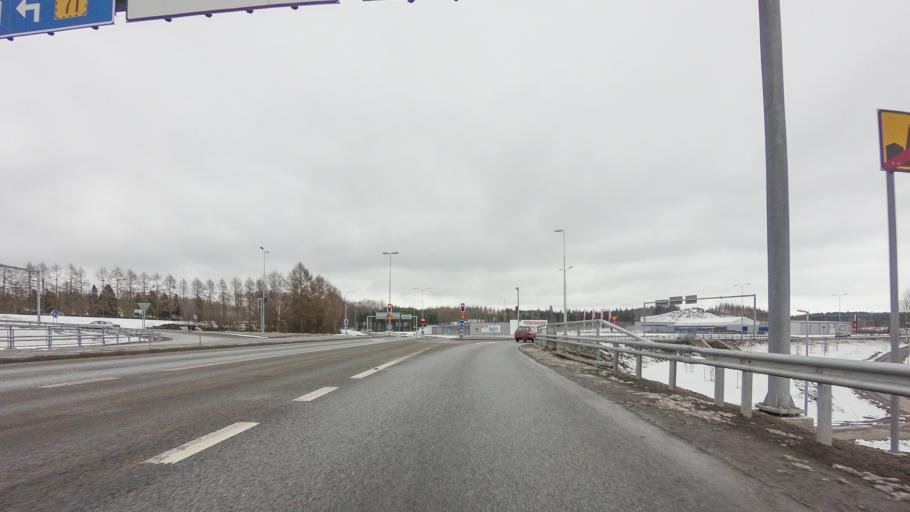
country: FI
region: Southern Savonia
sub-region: Savonlinna
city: Savonlinna
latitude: 61.8757
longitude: 28.9521
